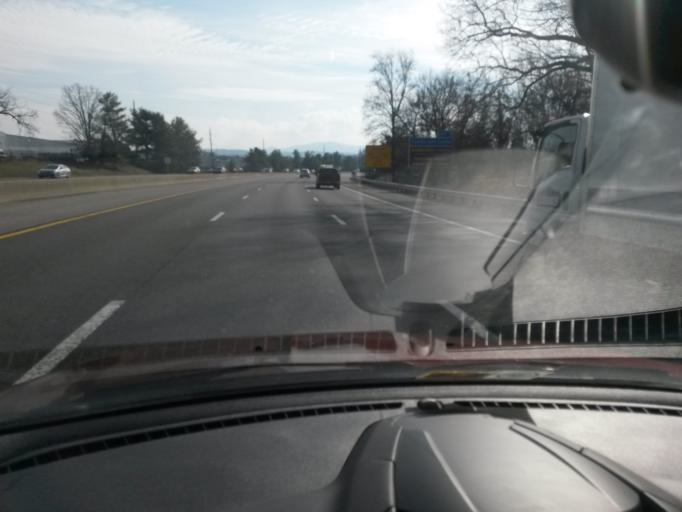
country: US
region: Virginia
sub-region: City of Roanoke
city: Roanoke
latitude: 37.2903
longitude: -79.9416
